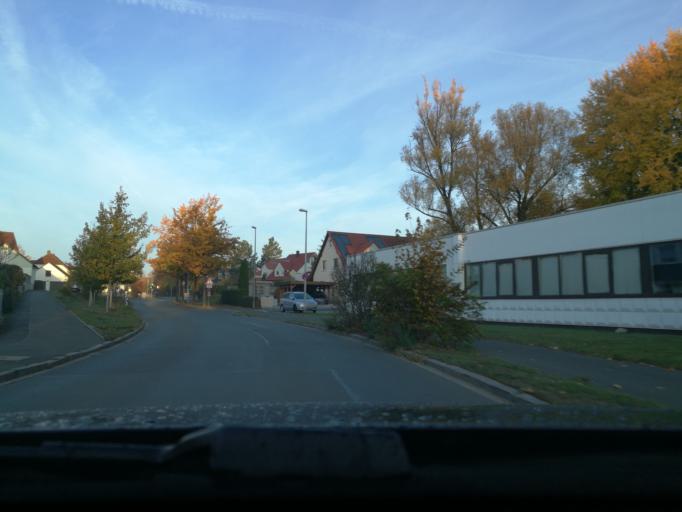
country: DE
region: Bavaria
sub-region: Regierungsbezirk Mittelfranken
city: Herzogenaurach
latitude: 49.5667
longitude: 10.9156
